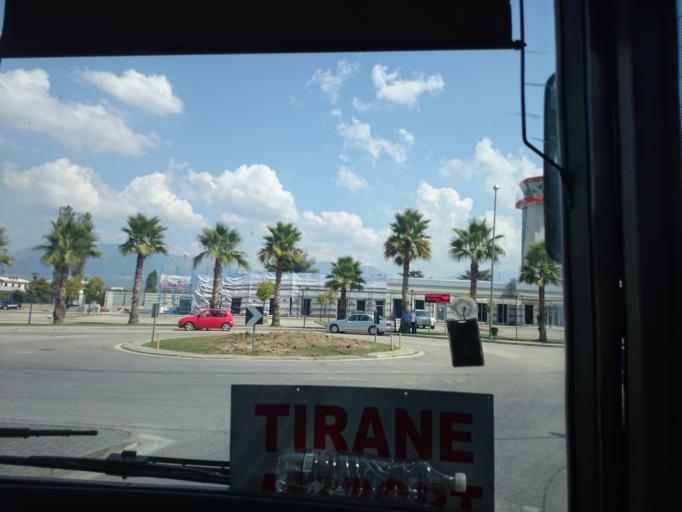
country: AL
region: Tirane
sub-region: Rrethi i Tiranes
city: Preze
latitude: 41.4210
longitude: 19.7121
